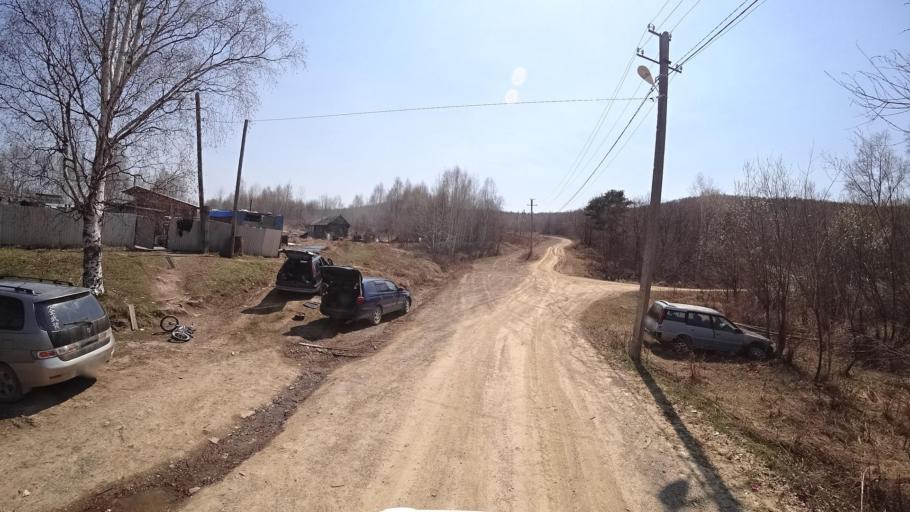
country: RU
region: Khabarovsk Krai
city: Selikhino
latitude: 50.6665
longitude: 137.4046
